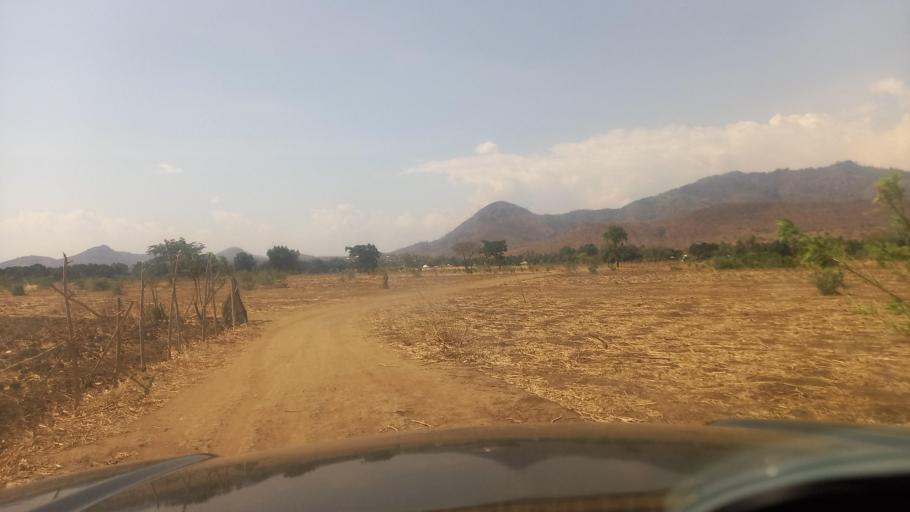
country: TZ
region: Morogoro
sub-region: Kilosa
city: Magole
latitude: -6.3302
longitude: 37.3825
